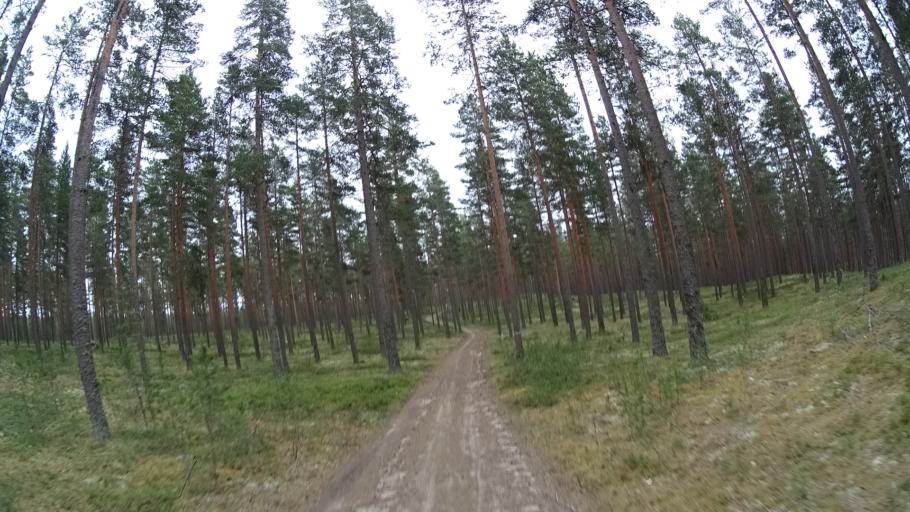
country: FI
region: Satakunta
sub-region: Pohjois-Satakunta
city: Jaemijaervi
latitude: 61.7641
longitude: 22.7680
